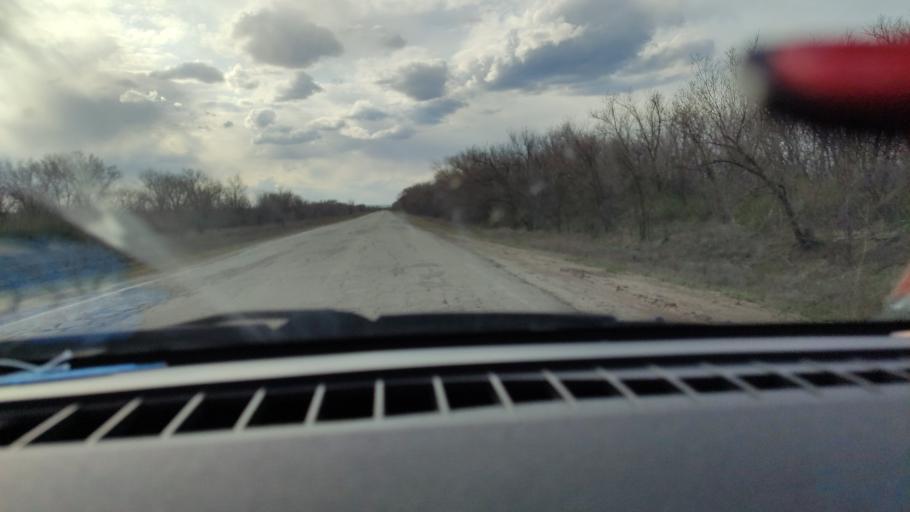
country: RU
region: Saratov
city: Rovnoye
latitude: 51.0689
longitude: 45.9957
